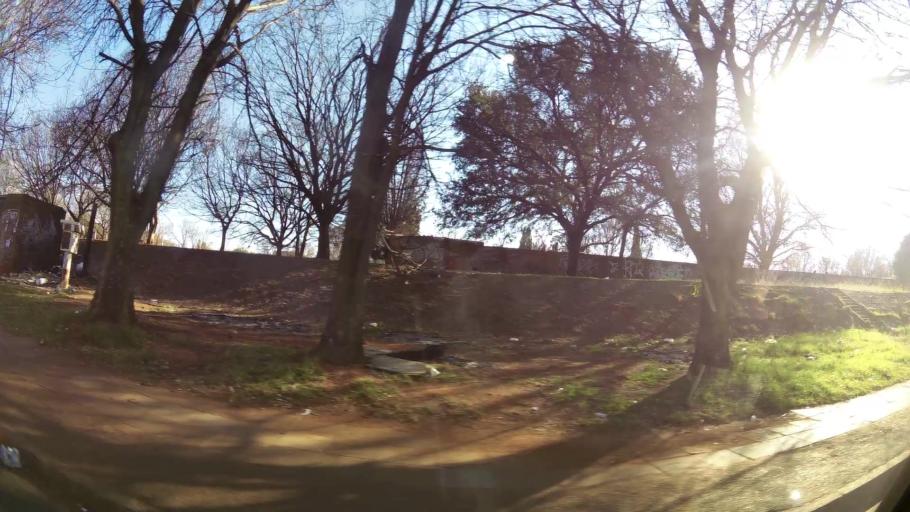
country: ZA
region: Gauteng
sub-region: City of Johannesburg Metropolitan Municipality
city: Johannesburg
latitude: -26.2060
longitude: 28.0741
